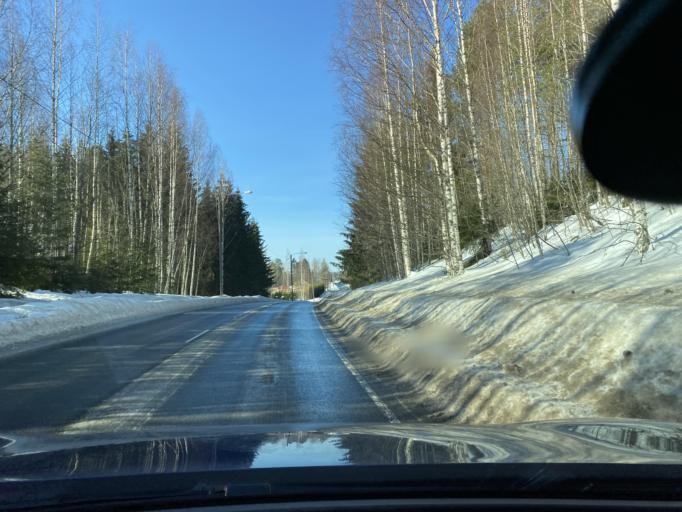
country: FI
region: Central Finland
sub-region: Joutsa
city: Joutsa
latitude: 61.8104
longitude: 25.9639
